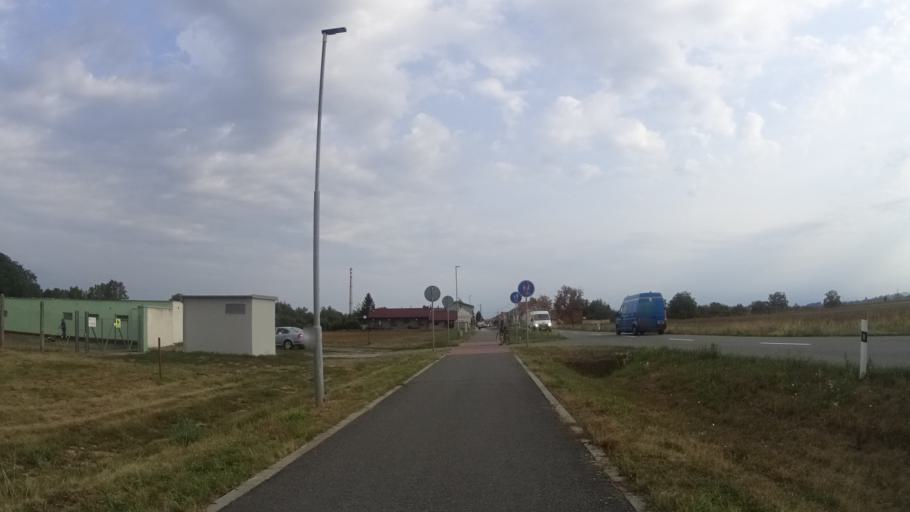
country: CZ
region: Zlin
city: Chropyne
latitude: 49.3488
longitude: 17.3752
